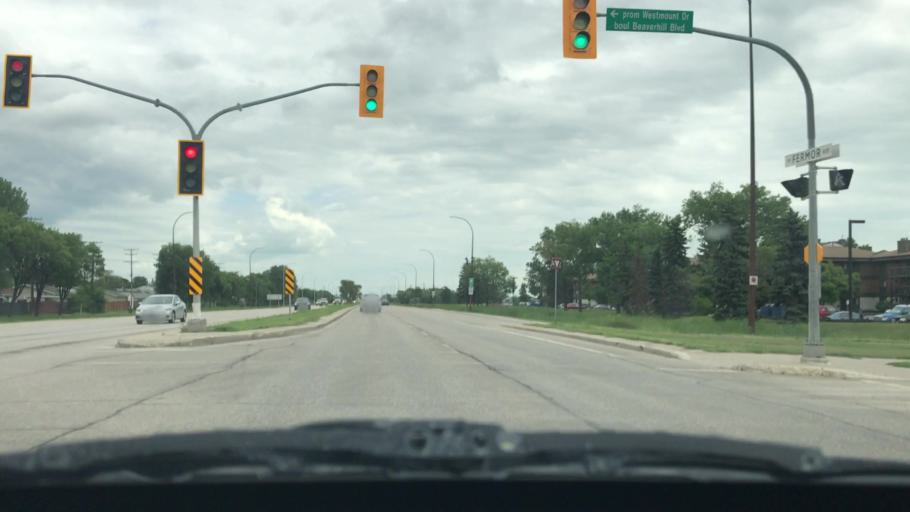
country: CA
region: Manitoba
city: Winnipeg
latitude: 49.8559
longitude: -97.0652
